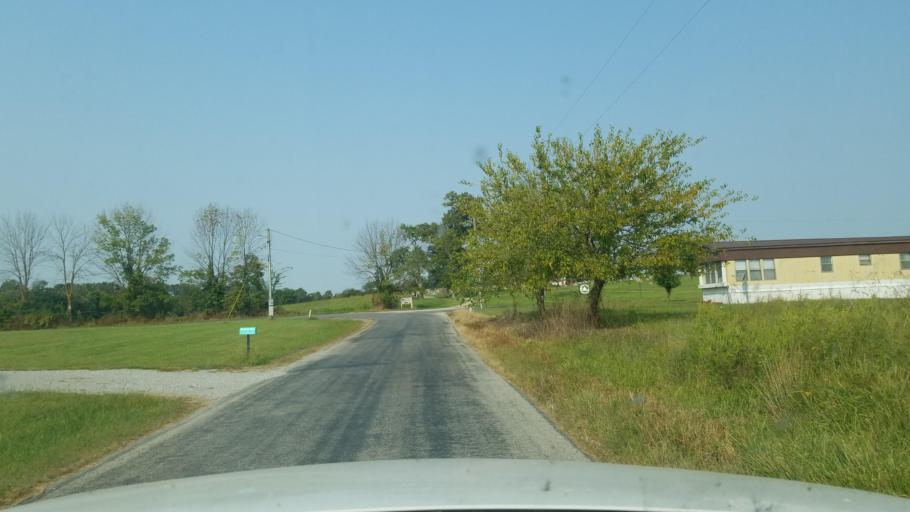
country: US
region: Illinois
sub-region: Saline County
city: Carrier Mills
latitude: 37.7942
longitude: -88.6600
